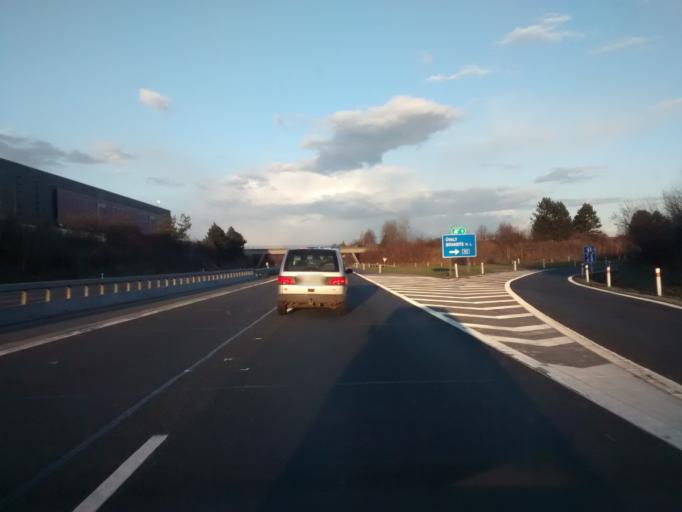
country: CZ
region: Central Bohemia
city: Jirny
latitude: 50.1223
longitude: 14.7010
